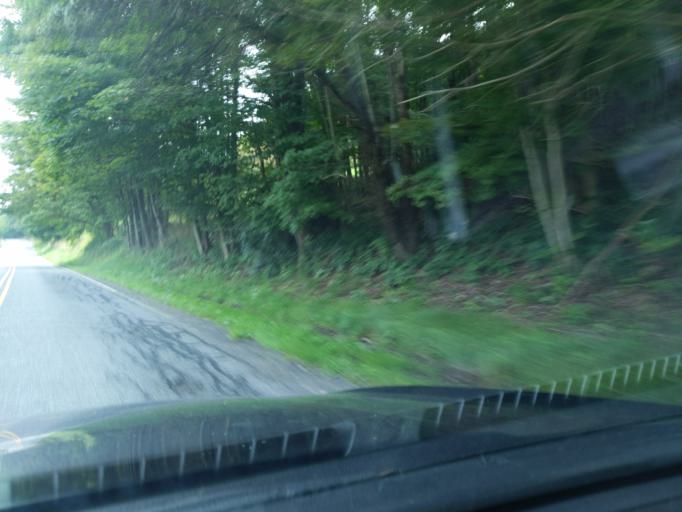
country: US
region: Pennsylvania
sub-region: Blair County
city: Claysburg
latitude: 40.3648
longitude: -78.5147
